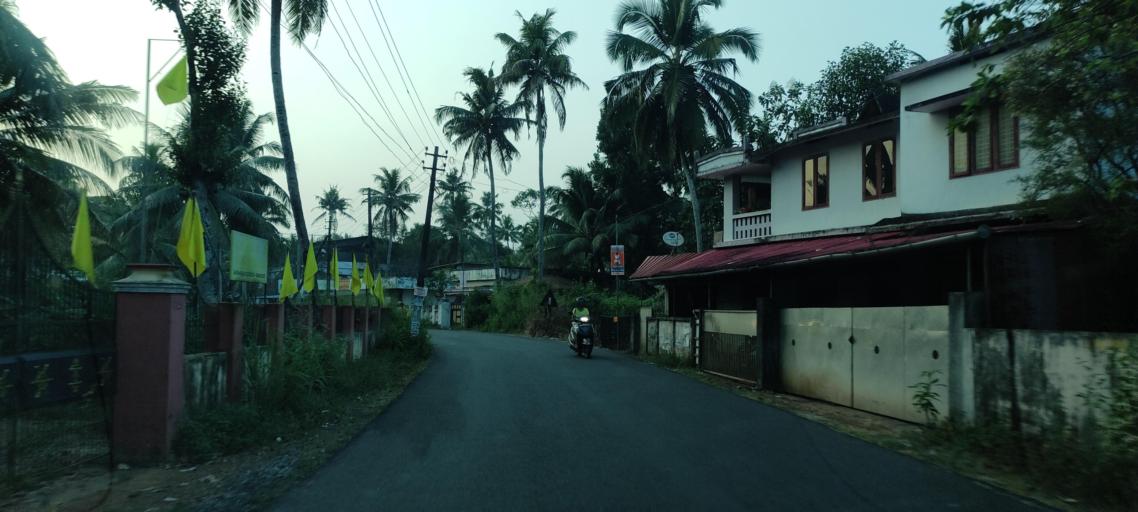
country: IN
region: Kerala
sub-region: Alappuzha
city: Kayankulam
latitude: 9.1368
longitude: 76.5227
